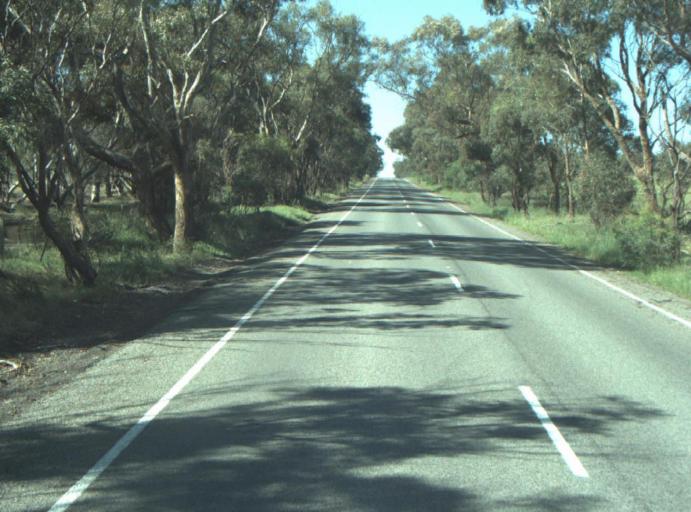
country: AU
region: Victoria
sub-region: Wyndham
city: Little River
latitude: -37.8997
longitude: 144.4005
